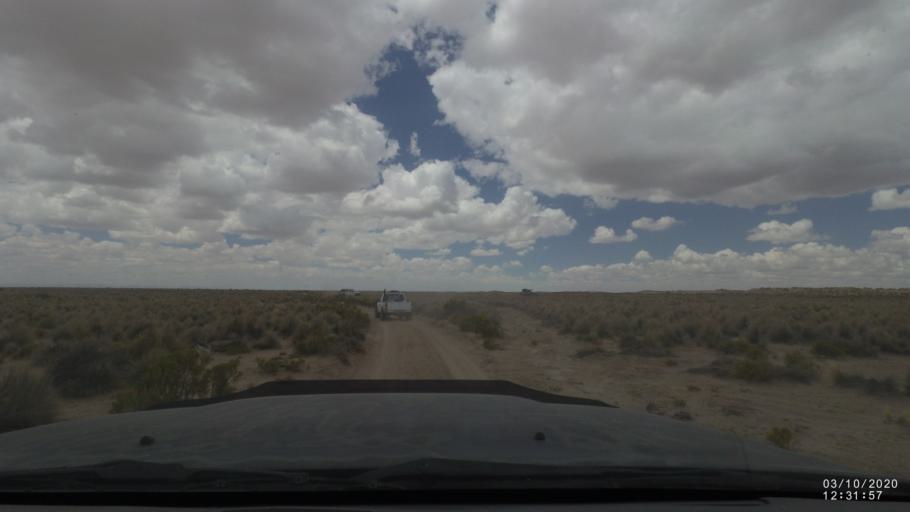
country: BO
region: Oruro
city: Poopo
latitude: -18.6872
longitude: -67.5365
